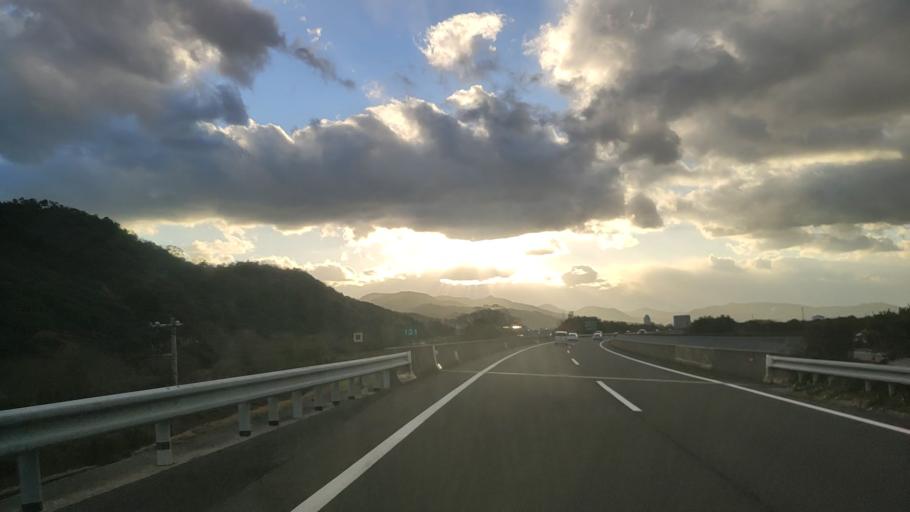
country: JP
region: Ehime
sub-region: Shikoku-chuo Shi
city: Matsuyama
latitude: 33.7895
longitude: 132.8942
